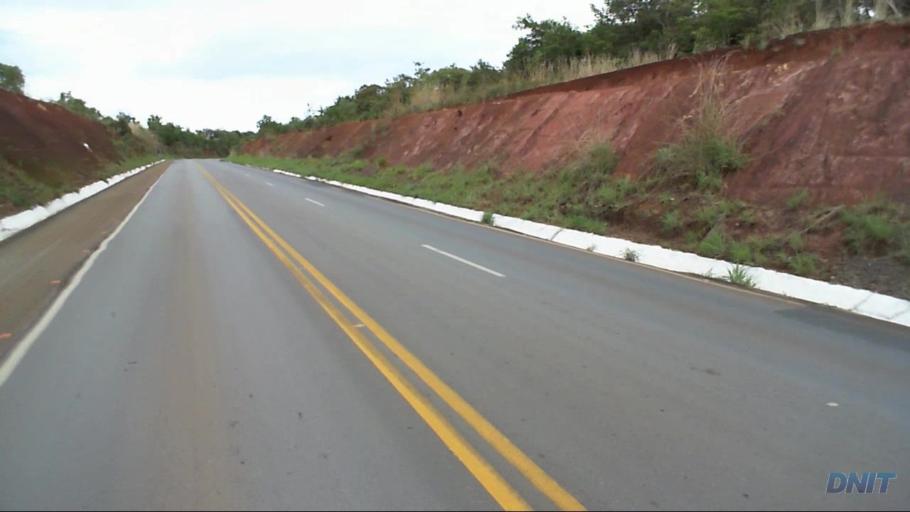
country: BR
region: Goias
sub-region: Barro Alto
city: Barro Alto
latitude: -14.8679
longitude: -49.0115
